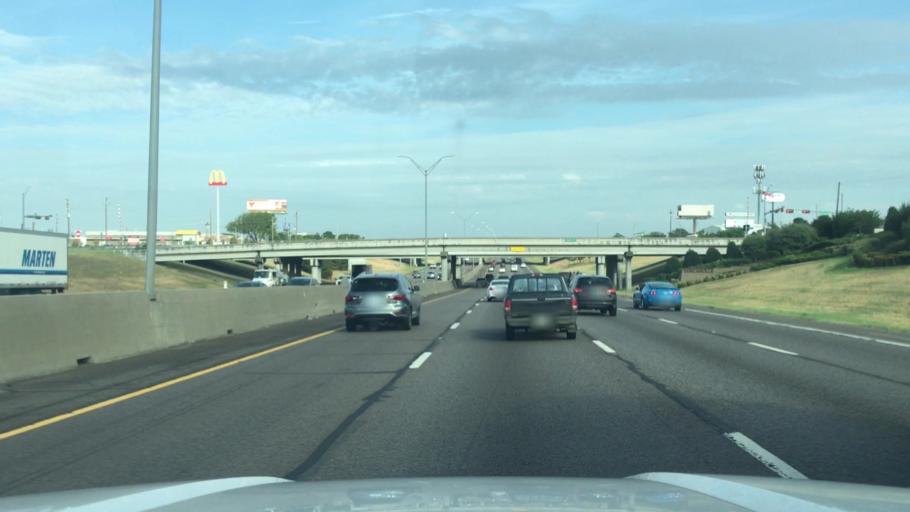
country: US
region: Texas
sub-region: Dallas County
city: Duncanville
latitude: 32.6646
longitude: -96.9045
